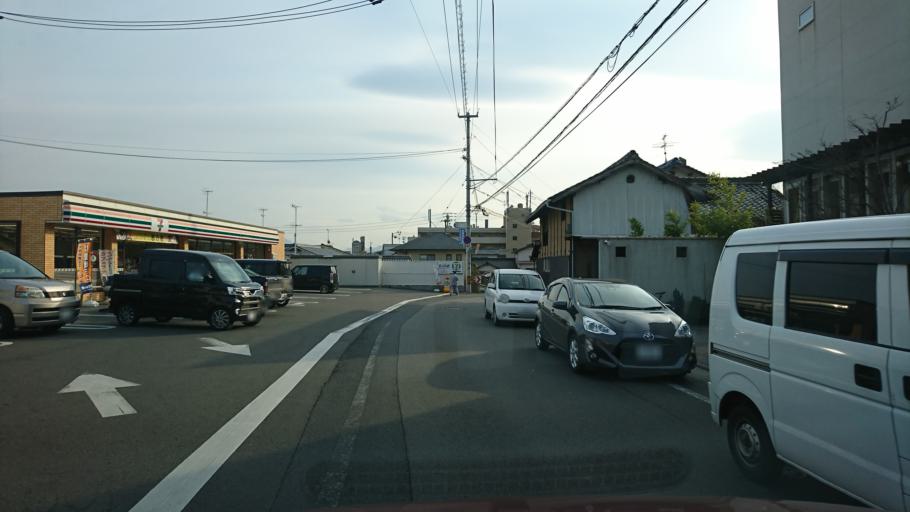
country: JP
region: Ehime
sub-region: Shikoku-chuo Shi
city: Matsuyama
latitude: 33.8582
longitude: 132.7769
